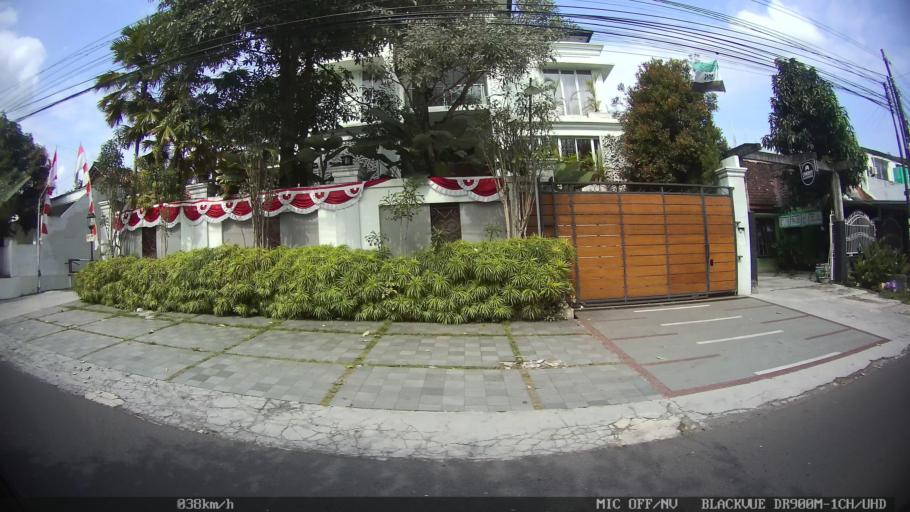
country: ID
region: Daerah Istimewa Yogyakarta
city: Depok
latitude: -7.7423
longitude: 110.4193
